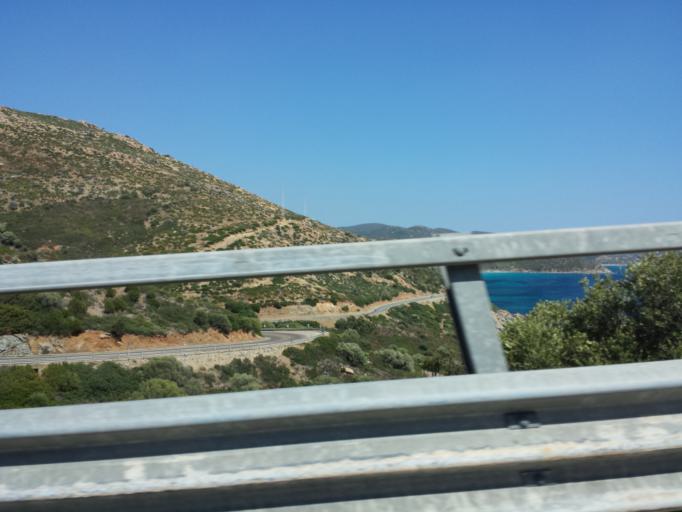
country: IT
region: Sardinia
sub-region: Provincia di Cagliari
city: Quartu Sant'Elena
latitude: 39.1809
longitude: 9.3523
